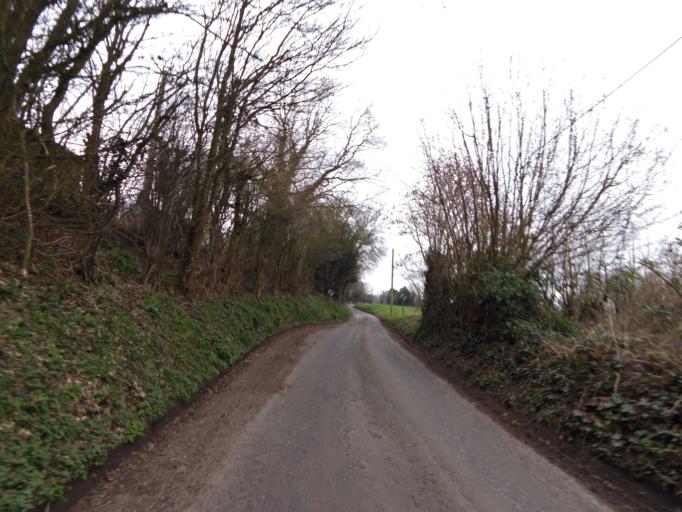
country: GB
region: England
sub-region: Suffolk
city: Cookley
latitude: 52.2701
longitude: 1.4496
